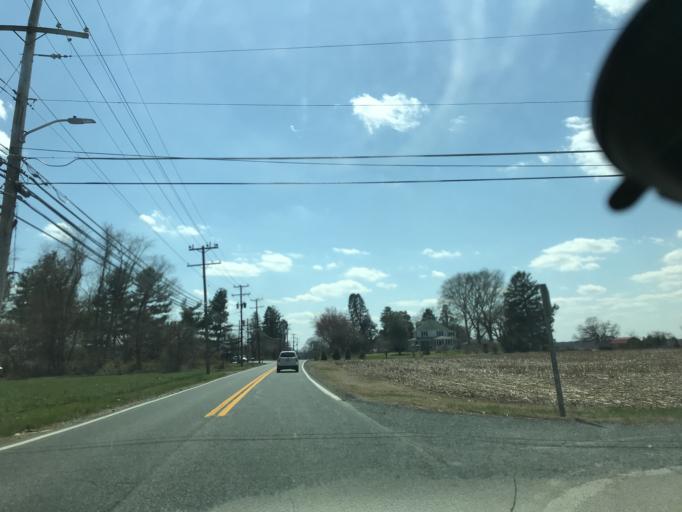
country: US
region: Maryland
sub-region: Harford County
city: Perryman
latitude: 39.4666
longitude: -76.2045
